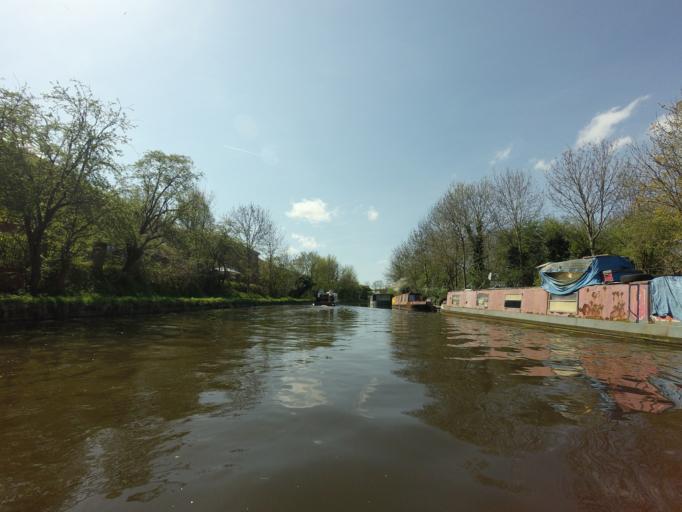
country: GB
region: England
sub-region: Greater London
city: Southall
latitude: 51.5168
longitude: -0.3842
